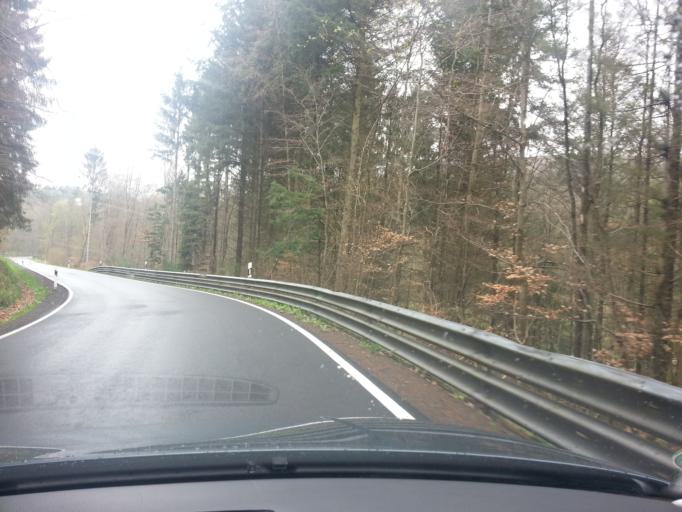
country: DE
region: Rheinland-Pfalz
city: Kashofen
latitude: 49.3200
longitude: 7.3892
